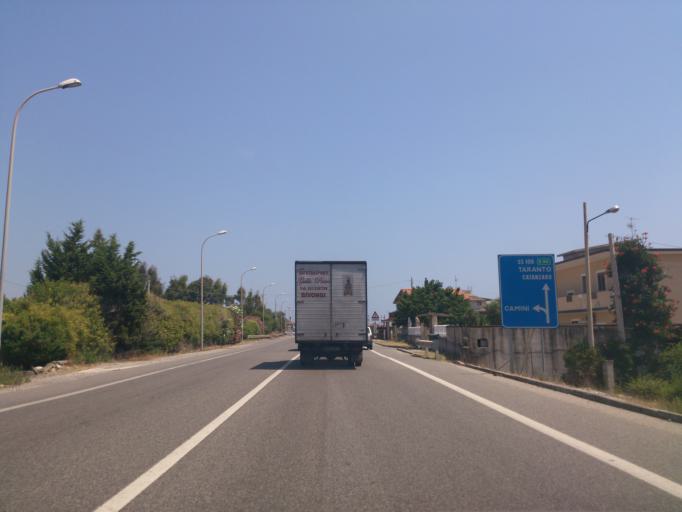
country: IT
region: Calabria
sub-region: Provincia di Reggio Calabria
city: Monasterace Marina
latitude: 38.4159
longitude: 16.5593
